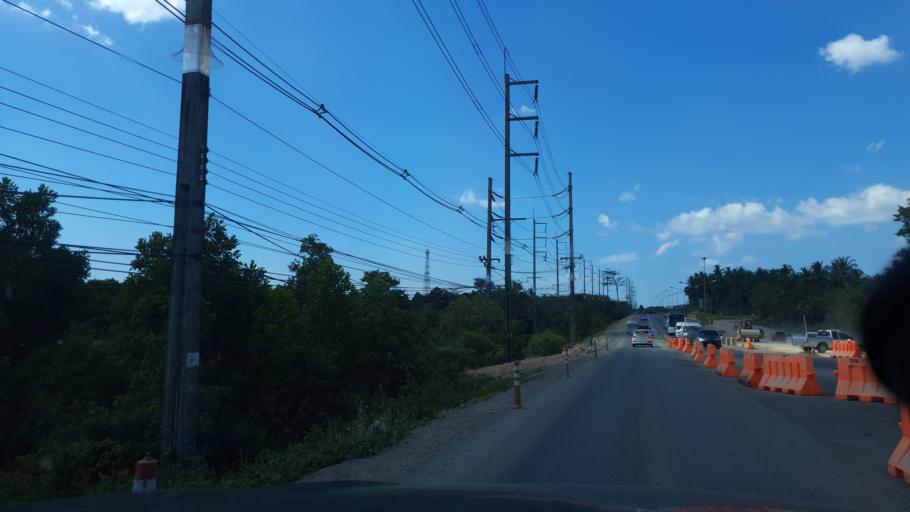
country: TH
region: Phangnga
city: Ban Khao Lak
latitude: 8.5340
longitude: 98.2834
